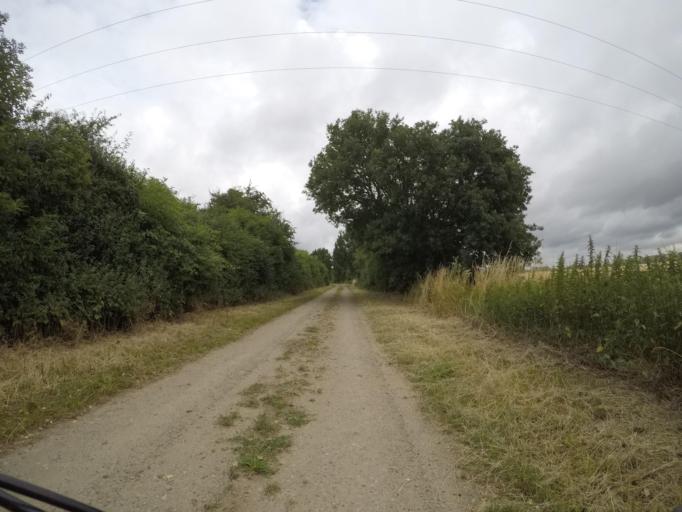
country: DE
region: Lower Saxony
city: Damnatz
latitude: 53.1650
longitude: 11.1150
